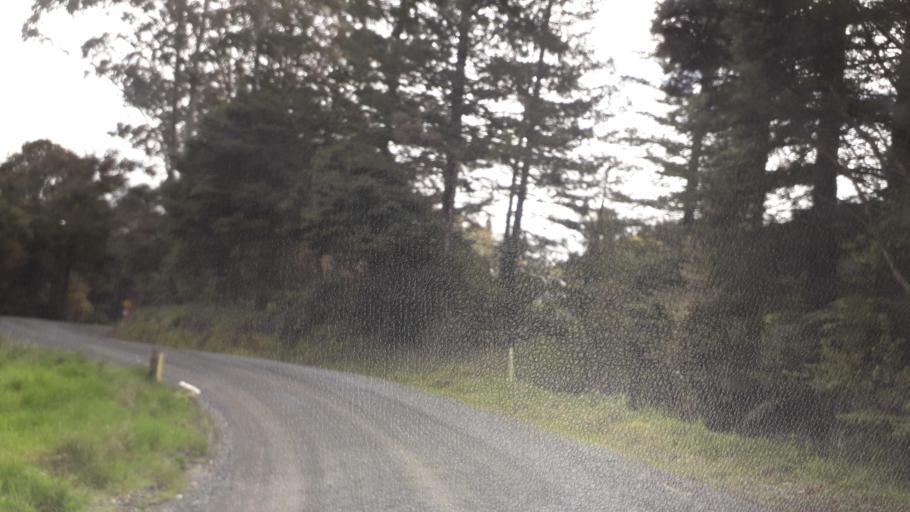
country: NZ
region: Northland
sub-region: Far North District
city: Taipa
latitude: -35.0945
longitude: 173.5320
